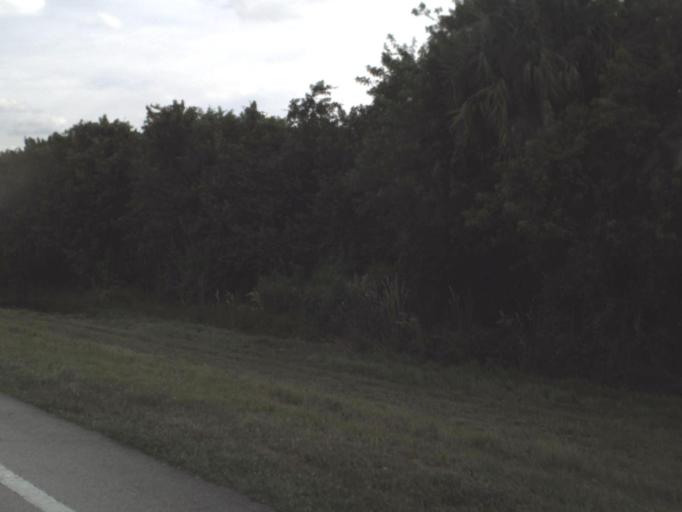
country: US
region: Florida
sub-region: Okeechobee County
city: Taylor Creek
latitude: 27.1662
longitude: -80.6881
